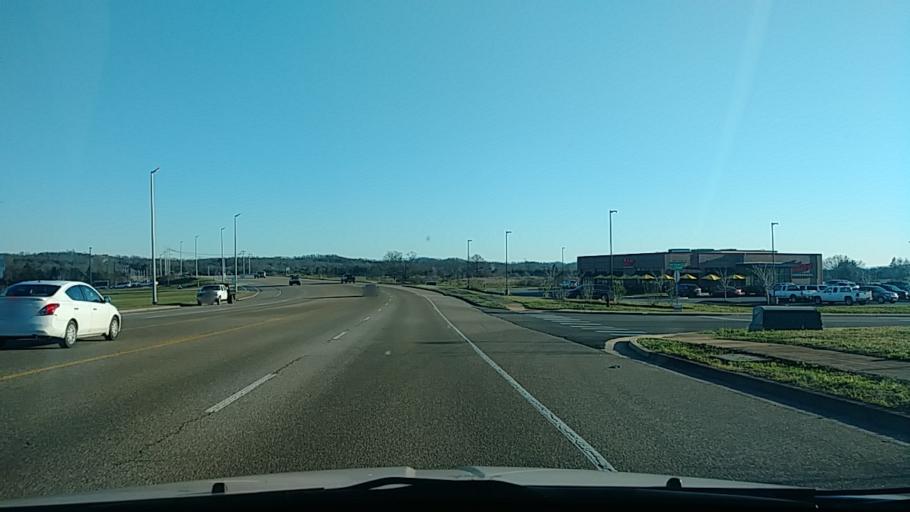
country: US
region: Tennessee
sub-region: Hamblen County
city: Morristown
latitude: 36.1908
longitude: -83.3593
